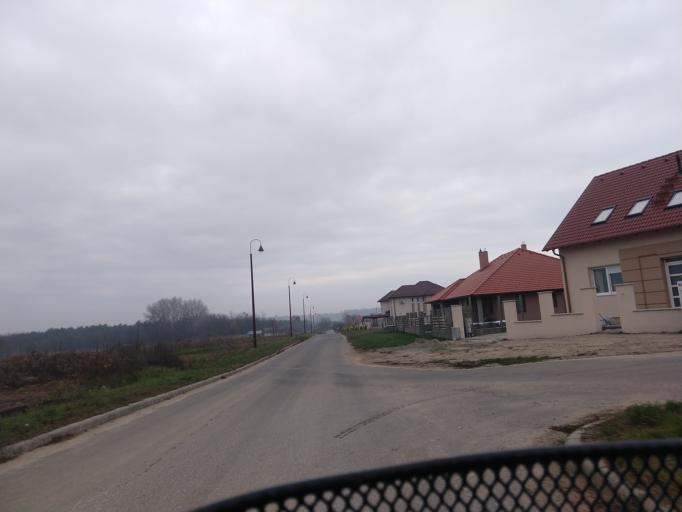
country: HU
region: Pest
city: Orbottyan
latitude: 47.6631
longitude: 19.2565
